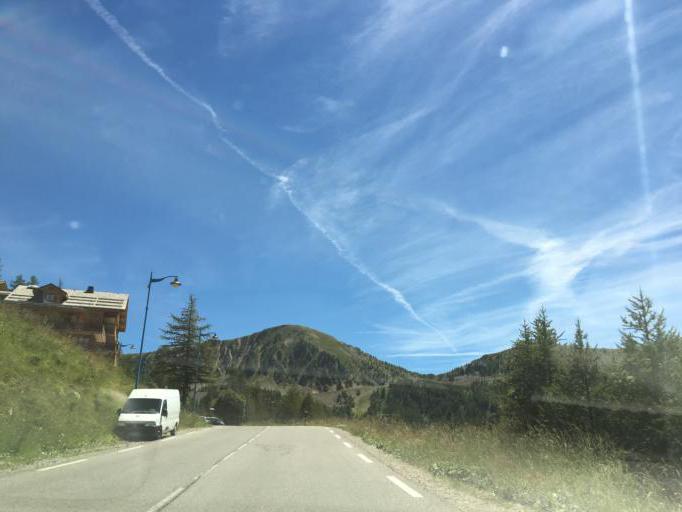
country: IT
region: Piedmont
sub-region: Provincia di Cuneo
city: Vinadio
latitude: 44.1868
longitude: 7.1605
